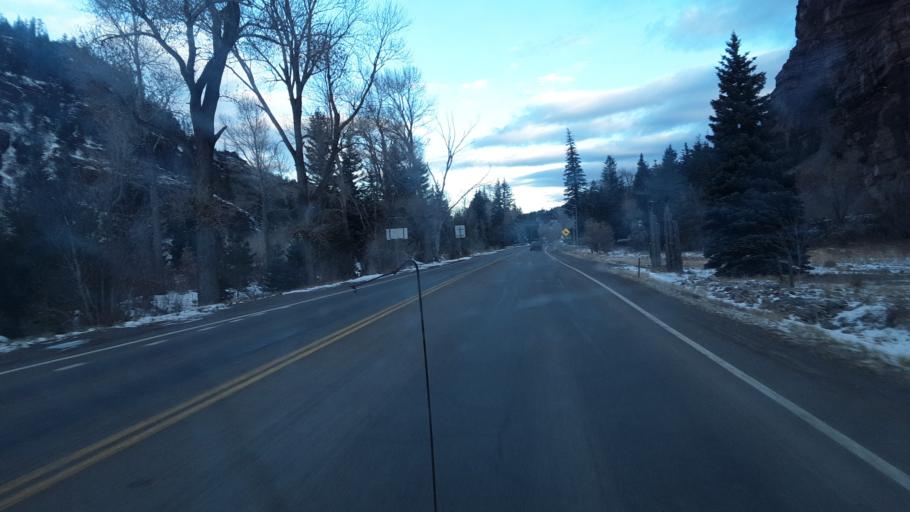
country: US
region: Colorado
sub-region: Ouray County
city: Ouray
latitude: 38.0406
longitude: -107.6799
